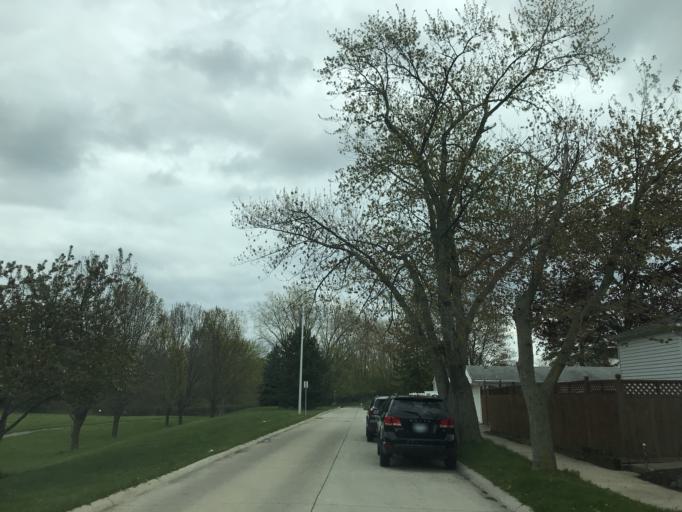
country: US
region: Michigan
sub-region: Wayne County
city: Riverview
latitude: 42.1819
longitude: -83.1782
